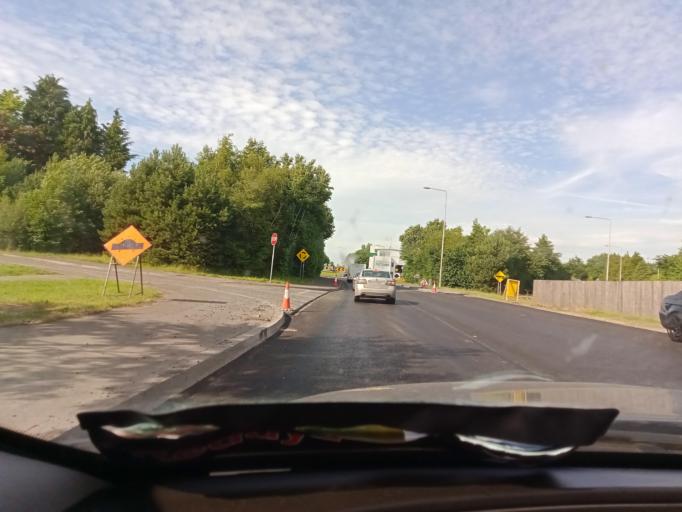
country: IE
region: Leinster
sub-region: An Iarmhi
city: An Muileann gCearr
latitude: 53.5207
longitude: -7.3036
